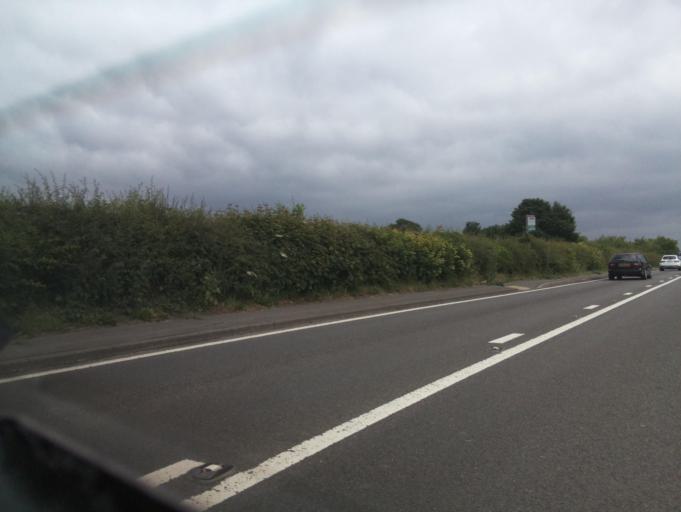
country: GB
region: England
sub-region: Derbyshire
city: Yeldersley
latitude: 52.9841
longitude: -1.6711
